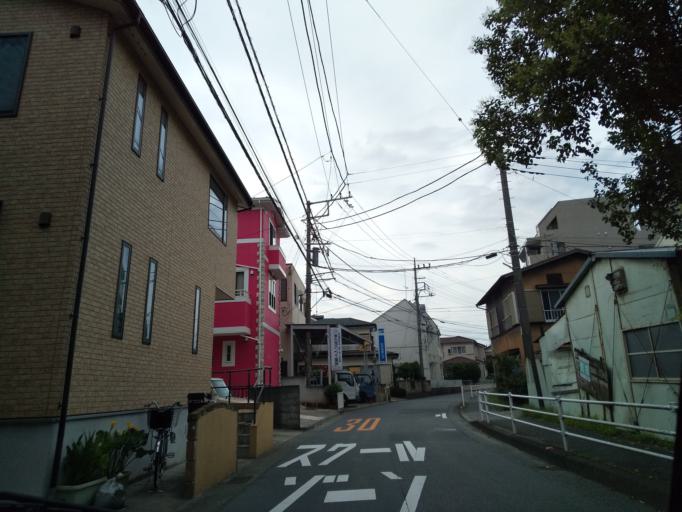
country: JP
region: Kanagawa
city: Atsugi
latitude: 35.4661
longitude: 139.3613
